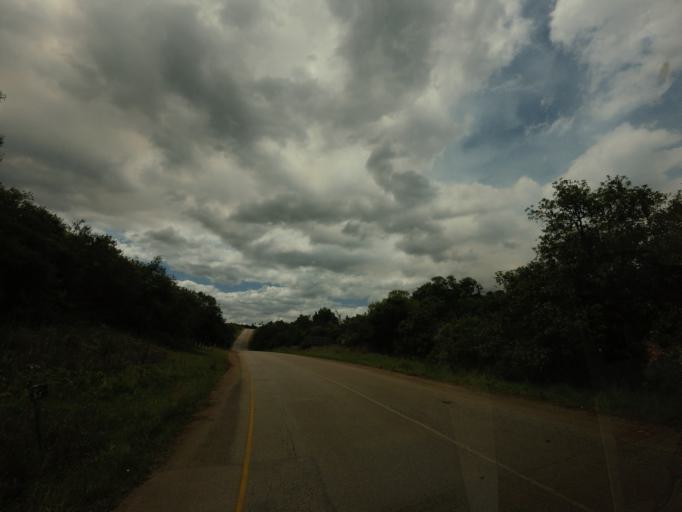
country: ZA
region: Mpumalanga
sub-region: Ehlanzeni District
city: Graksop
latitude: -24.9302
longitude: 30.8103
